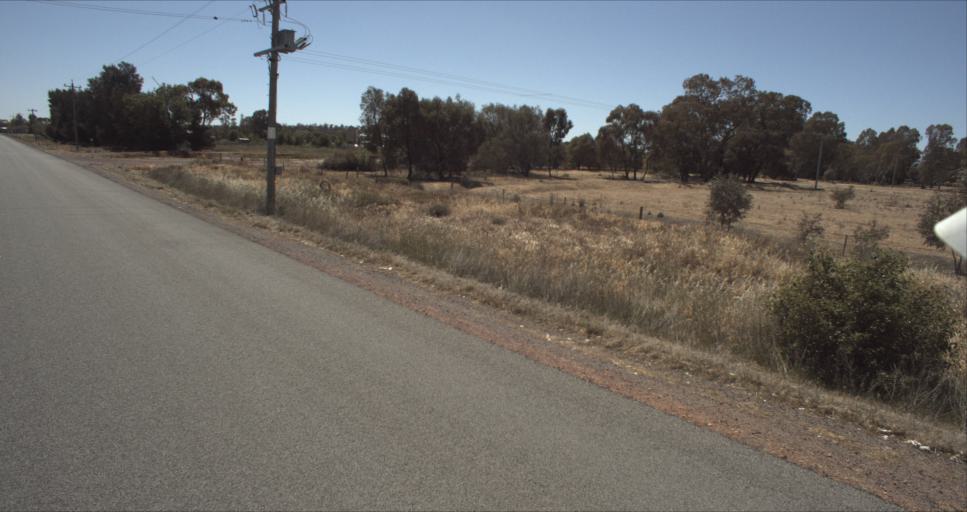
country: AU
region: New South Wales
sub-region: Leeton
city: Leeton
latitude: -34.4318
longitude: 146.2995
